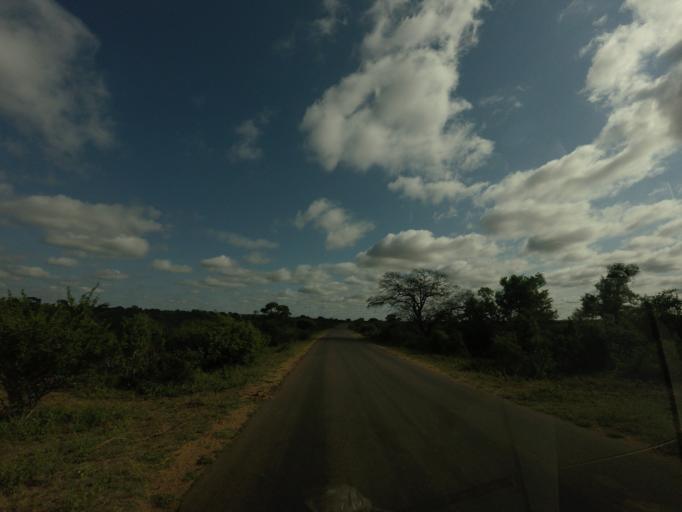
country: ZA
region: Mpumalanga
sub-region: Ehlanzeni District
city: Komatipoort
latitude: -25.1456
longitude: 31.9400
